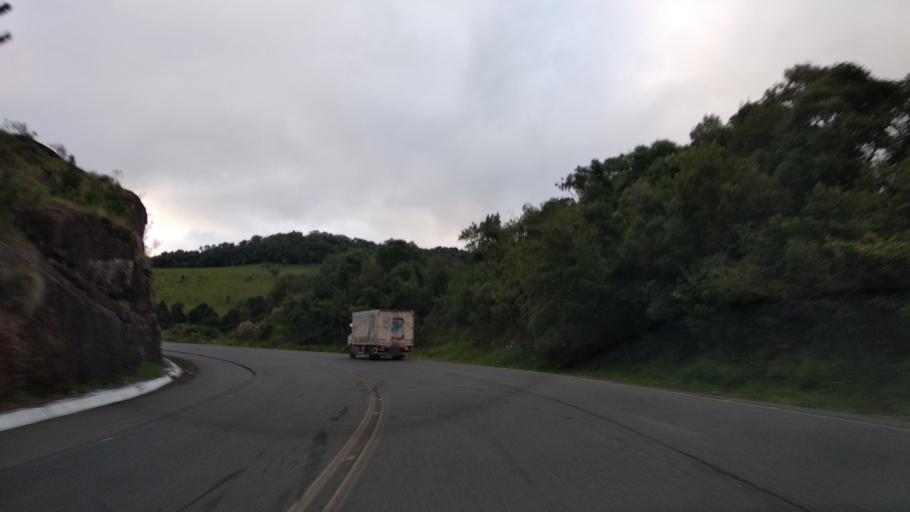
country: BR
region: Santa Catarina
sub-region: Campos Novos
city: Campos Novos
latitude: -27.4922
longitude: -50.9726
